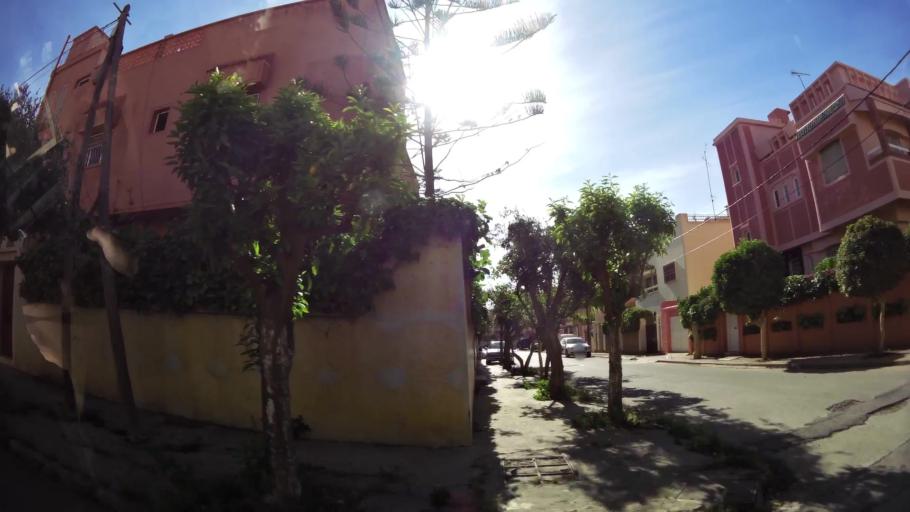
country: MA
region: Oriental
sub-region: Oujda-Angad
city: Oujda
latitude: 34.6675
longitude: -1.9056
